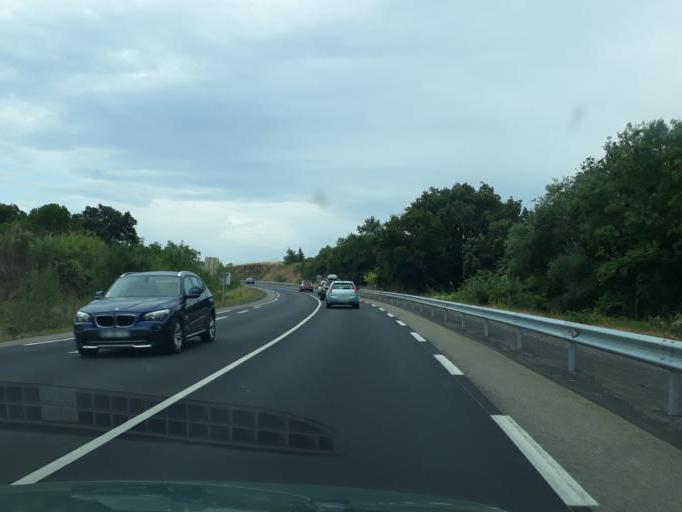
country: FR
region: Languedoc-Roussillon
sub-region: Departement de l'Herault
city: Saint-Thibery
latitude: 43.3915
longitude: 3.4132
